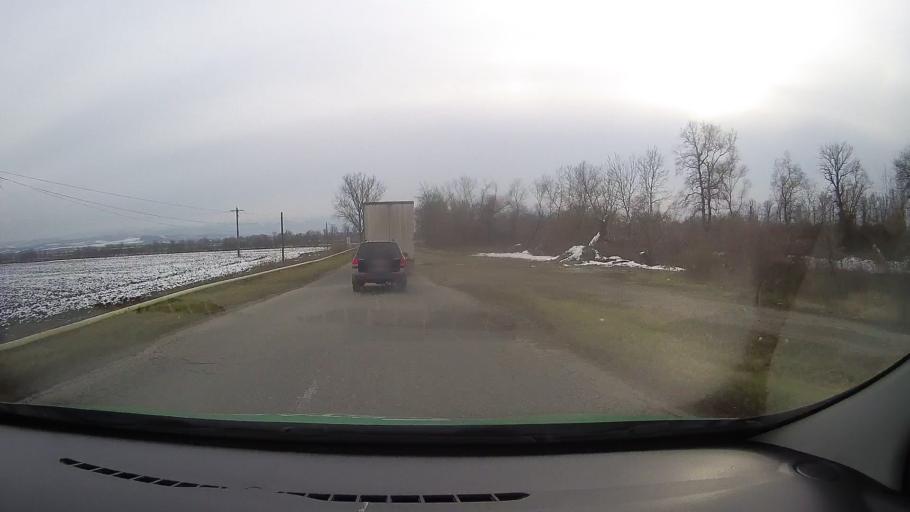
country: RO
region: Hunedoara
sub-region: Comuna Geoagiu
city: Geoagiu
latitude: 45.8981
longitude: 23.2255
